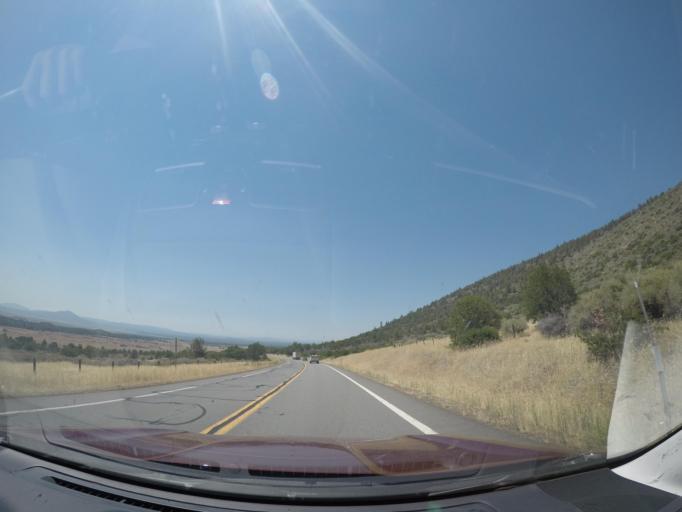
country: US
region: California
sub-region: Shasta County
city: Burney
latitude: 41.0908
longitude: -121.2699
